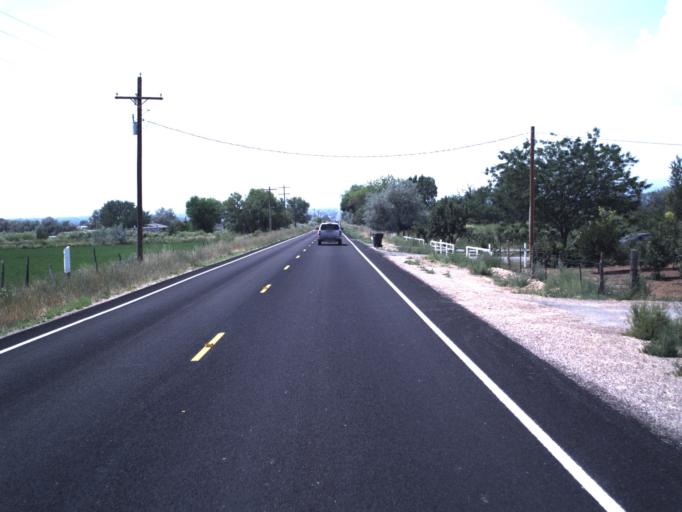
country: US
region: Utah
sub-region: Duchesne County
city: Roosevelt
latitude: 40.4037
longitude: -109.8054
